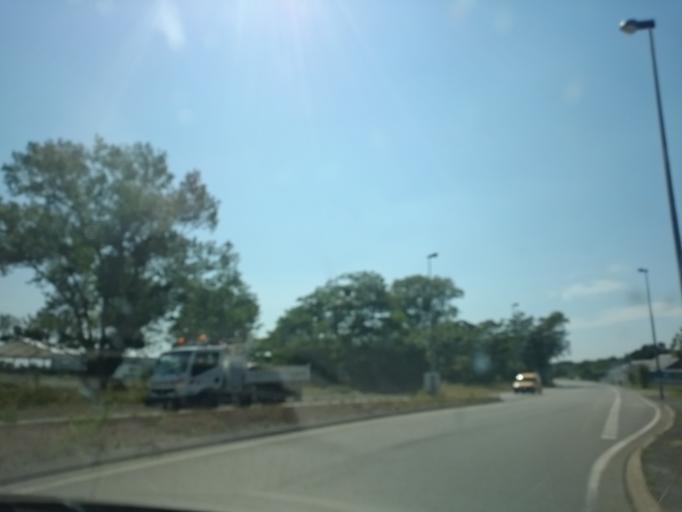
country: FR
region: Pays de la Loire
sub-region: Departement de la Loire-Atlantique
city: Coueron
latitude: 47.2095
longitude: -1.7010
